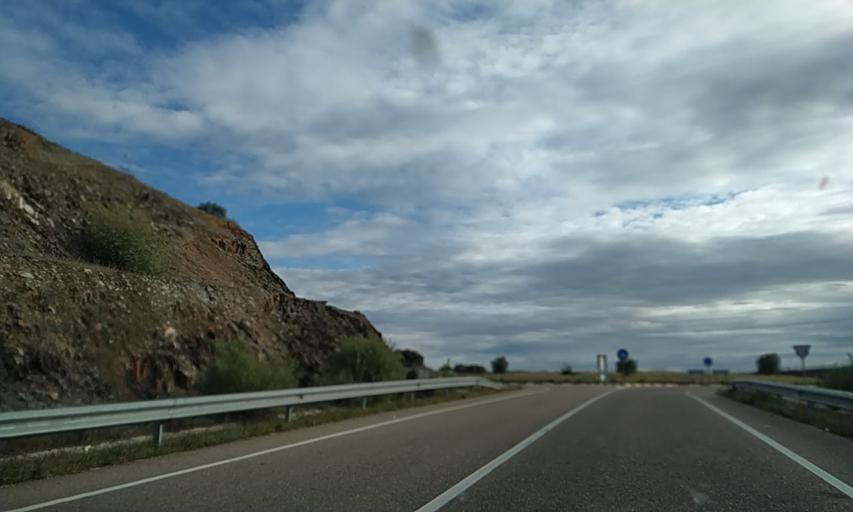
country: ES
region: Extremadura
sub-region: Provincia de Caceres
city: Casas de Don Gomez
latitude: 40.0272
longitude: -6.6119
